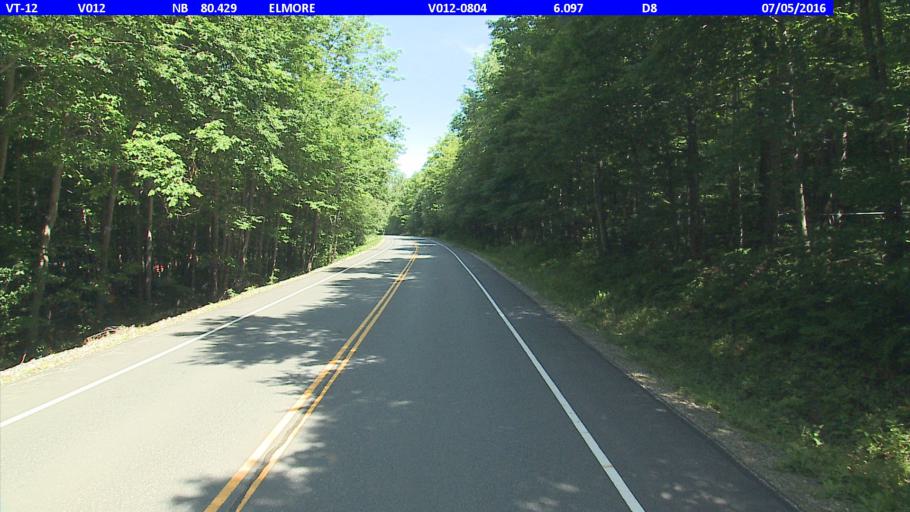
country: US
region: Vermont
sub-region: Lamoille County
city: Morrisville
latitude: 44.5321
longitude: -72.5186
